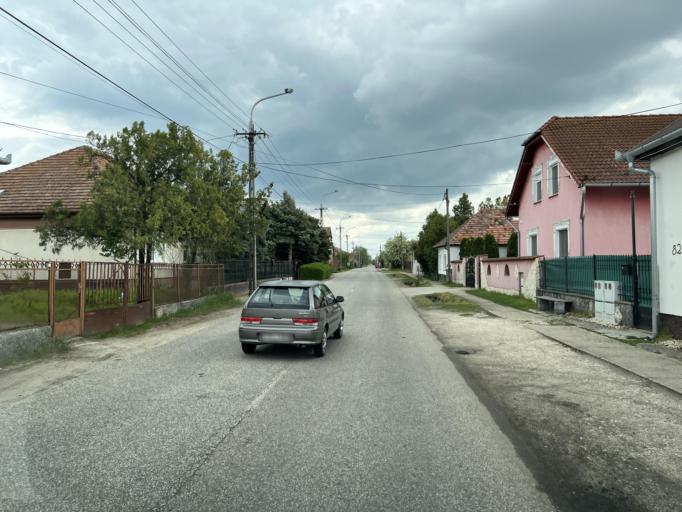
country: HU
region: Pest
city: Hernad
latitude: 47.1644
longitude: 19.4290
